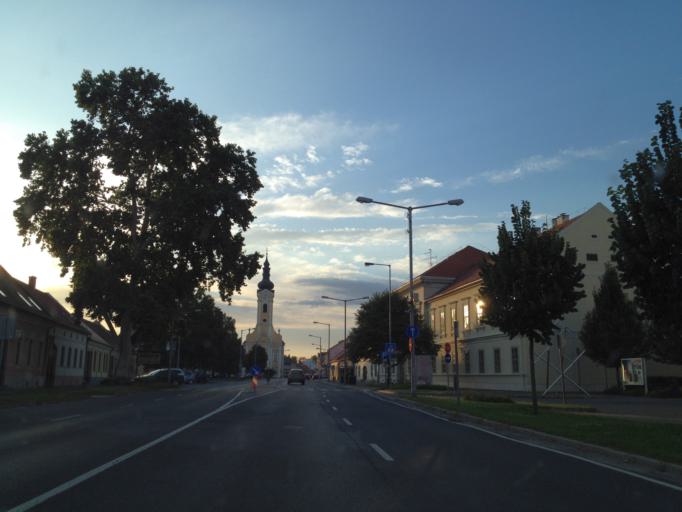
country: HU
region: Gyor-Moson-Sopron
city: Mosonmagyarovar
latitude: 47.8530
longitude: 17.2802
